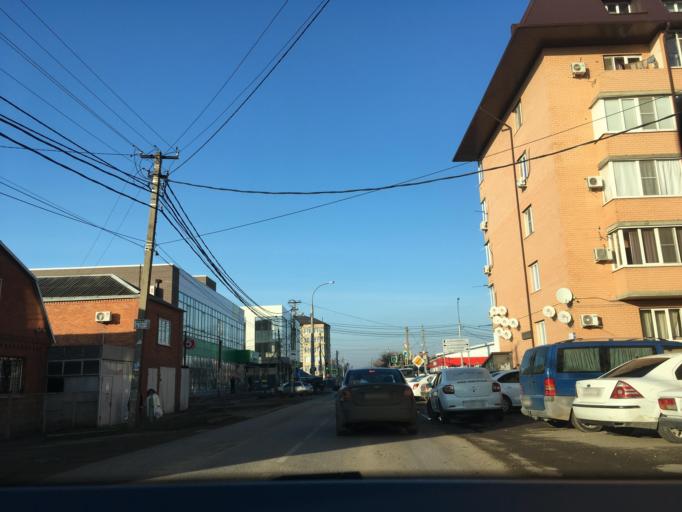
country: RU
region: Krasnodarskiy
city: Krasnodar
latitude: 45.0745
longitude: 39.0211
